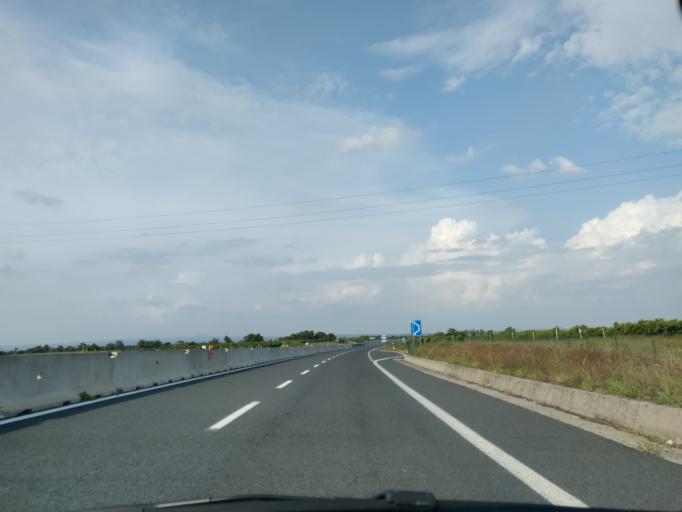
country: IT
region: Latium
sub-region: Provincia di Viterbo
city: Blera
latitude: 42.3552
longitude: 11.9829
